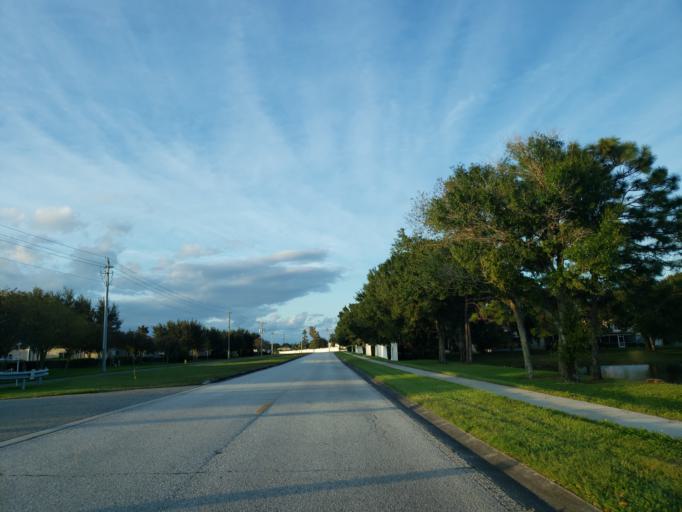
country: US
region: Florida
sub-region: Hillsborough County
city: Riverview
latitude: 27.7931
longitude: -82.3287
